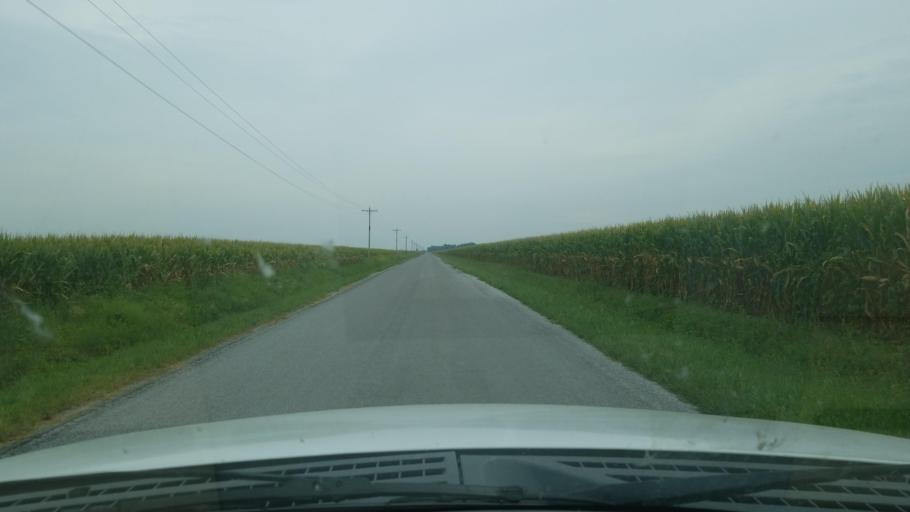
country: US
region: Illinois
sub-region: Saline County
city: Eldorado
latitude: 37.8669
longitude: -88.4684
